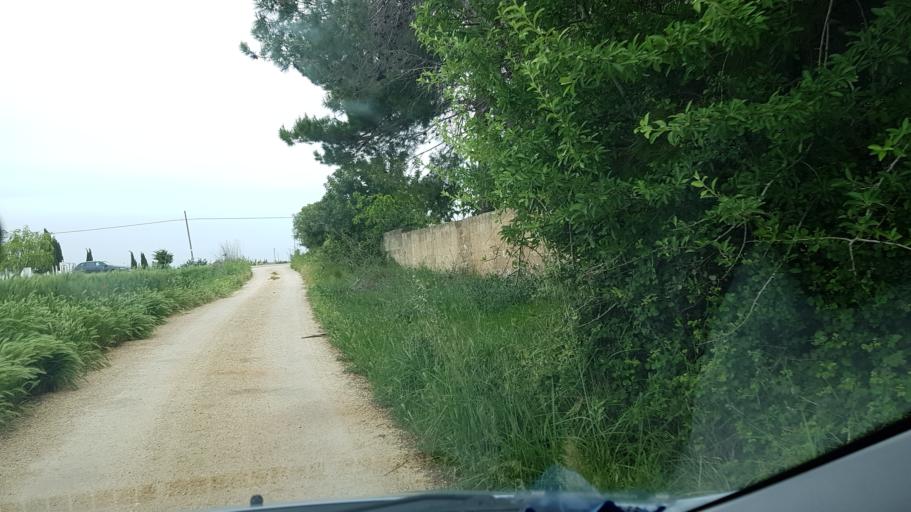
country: IT
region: Apulia
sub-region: Provincia di Brindisi
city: Brindisi
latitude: 40.6477
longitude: 17.8833
